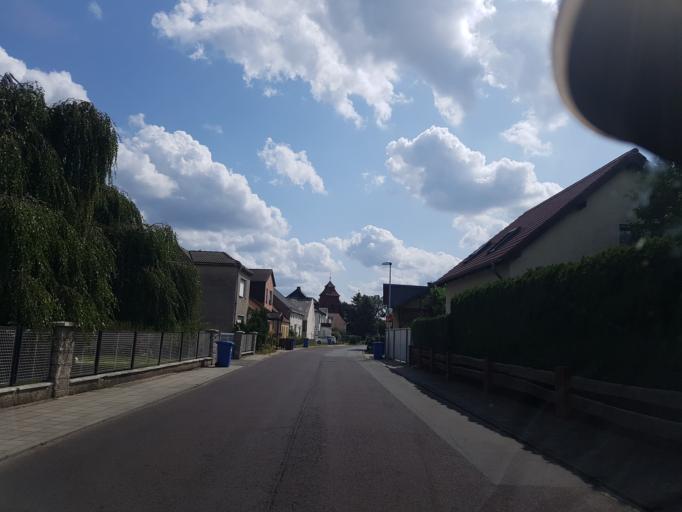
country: DE
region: Brandenburg
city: Gross Kreutz
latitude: 52.3386
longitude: 12.7228
